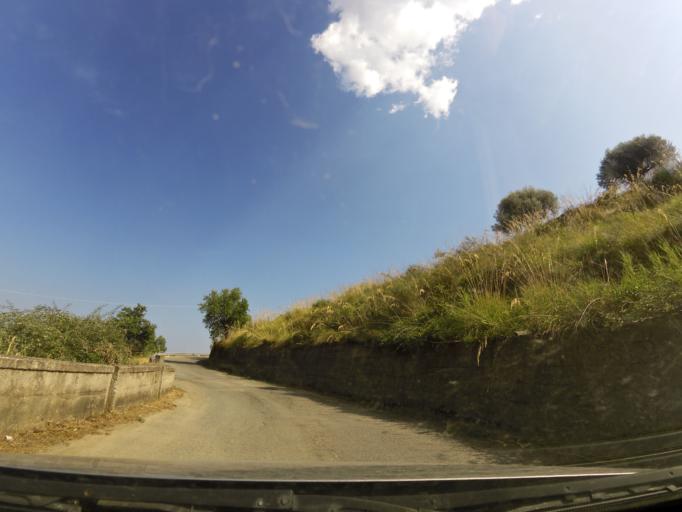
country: IT
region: Calabria
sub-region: Provincia di Reggio Calabria
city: Pazzano
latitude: 38.4657
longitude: 16.4528
